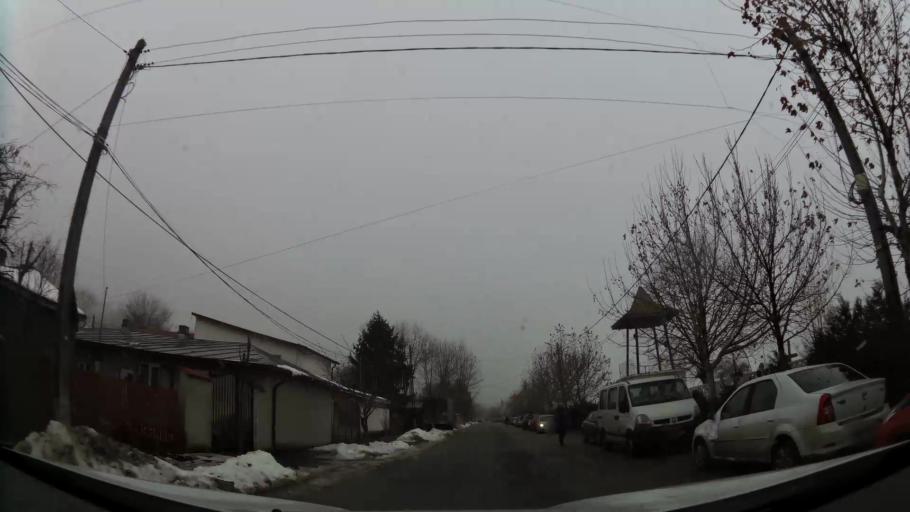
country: RO
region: Ilfov
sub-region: Comuna Chiajna
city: Rosu
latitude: 44.4549
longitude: 26.0081
